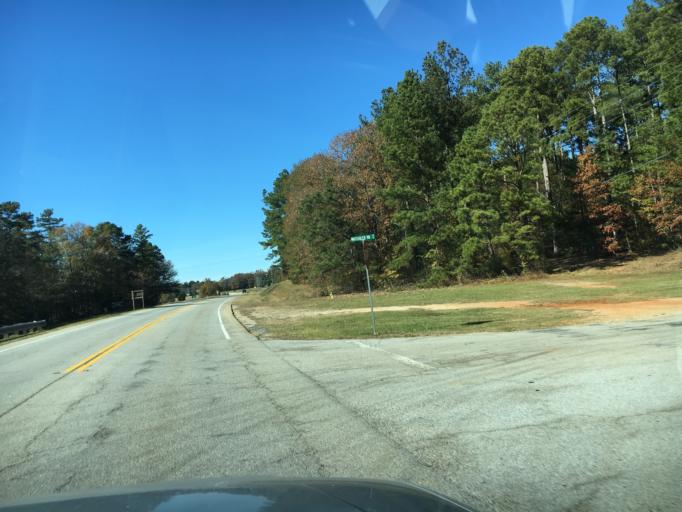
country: US
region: Georgia
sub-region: Hart County
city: Hartwell
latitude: 34.3385
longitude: -82.8445
